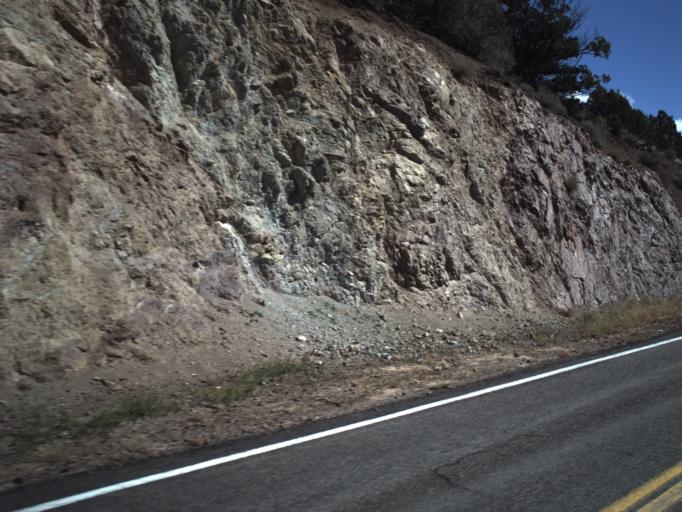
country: US
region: Utah
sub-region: Washington County
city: Enterprise
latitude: 37.5406
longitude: -113.6747
